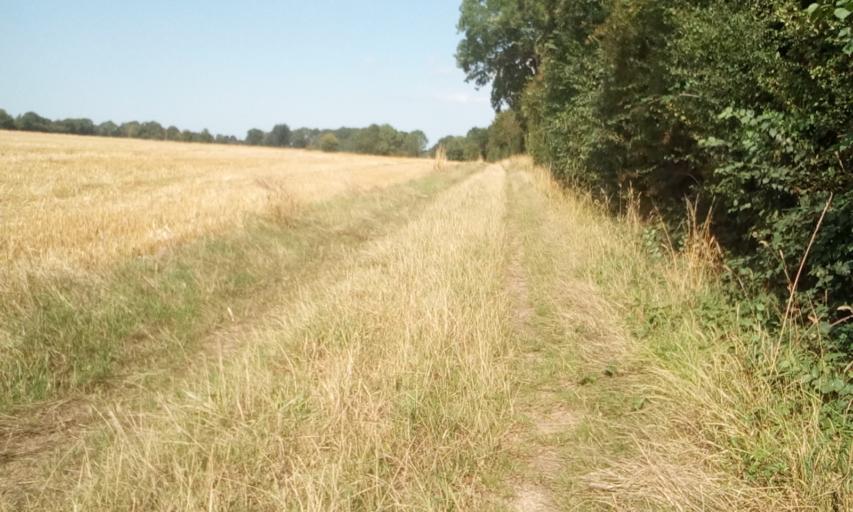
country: FR
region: Lower Normandy
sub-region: Departement du Calvados
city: Argences
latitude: 49.1358
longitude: -0.1142
